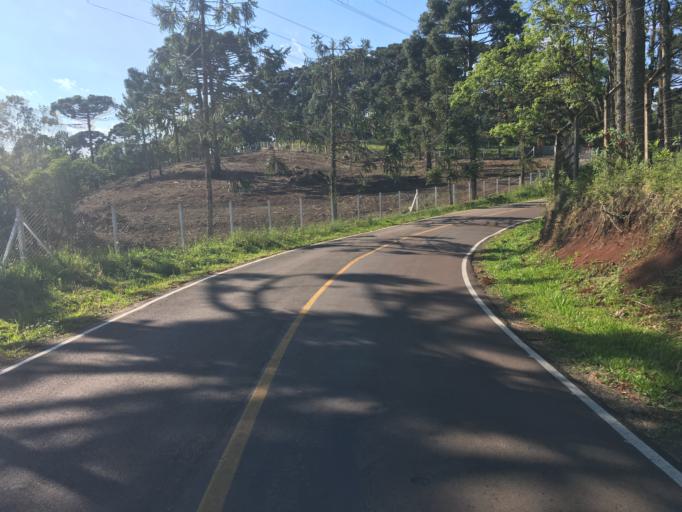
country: BR
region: Parana
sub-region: Campina Grande Do Sul
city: Campina Grande do Sul
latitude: -25.3172
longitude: -48.9972
